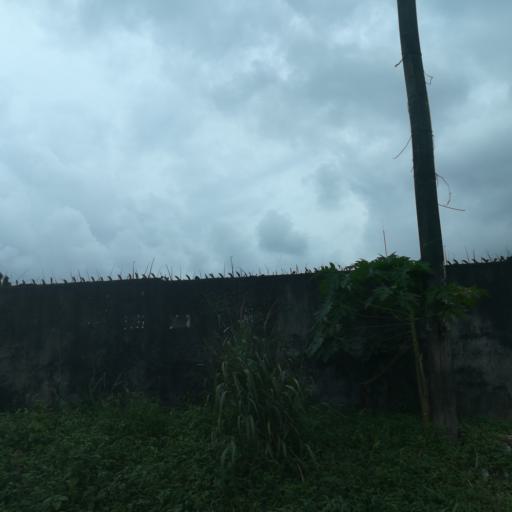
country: NG
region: Rivers
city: Port Harcourt
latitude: 4.8318
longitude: 7.0328
